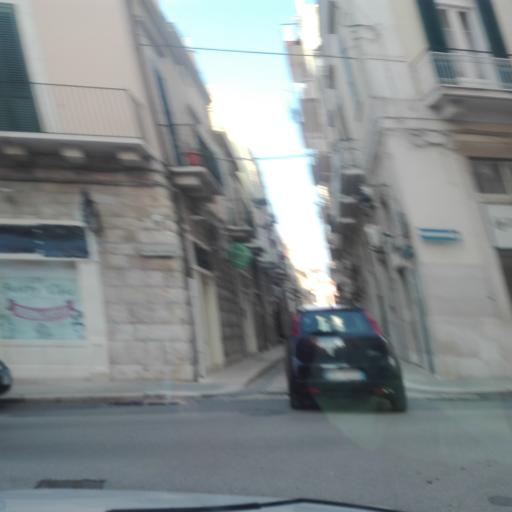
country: IT
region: Apulia
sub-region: Provincia di Bari
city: Corato
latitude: 41.1548
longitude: 16.4114
